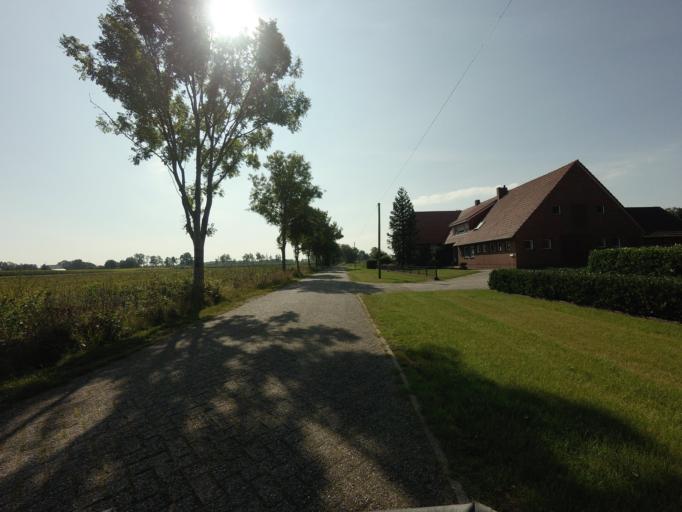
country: DE
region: Lower Saxony
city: Emlichheim
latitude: 52.5819
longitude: 6.8343
